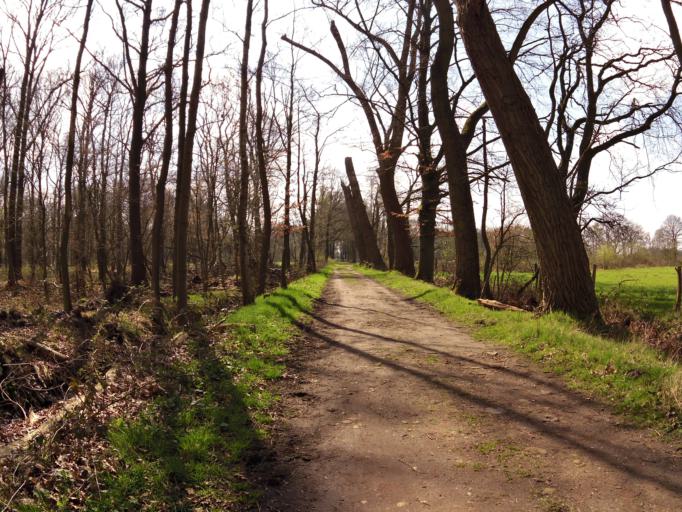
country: NL
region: North Brabant
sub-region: Gemeente Haaren
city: Haaren
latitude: 51.5561
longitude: 5.2660
